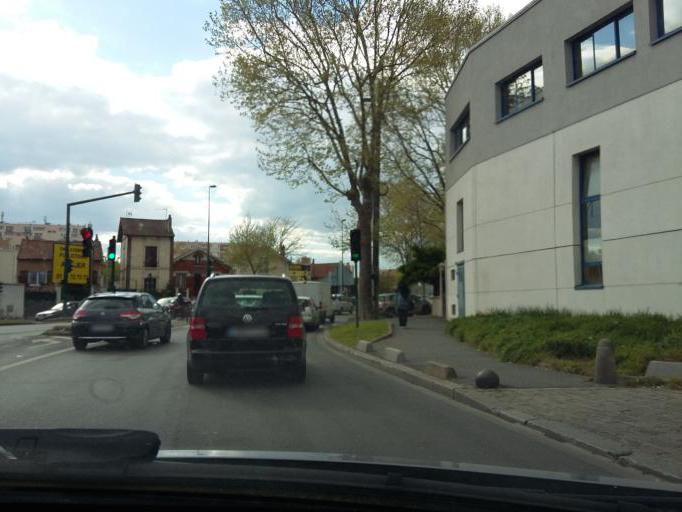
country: FR
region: Ile-de-France
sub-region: Departement de Seine-Saint-Denis
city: Epinay-sur-Seine
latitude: 48.9594
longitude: 2.3002
